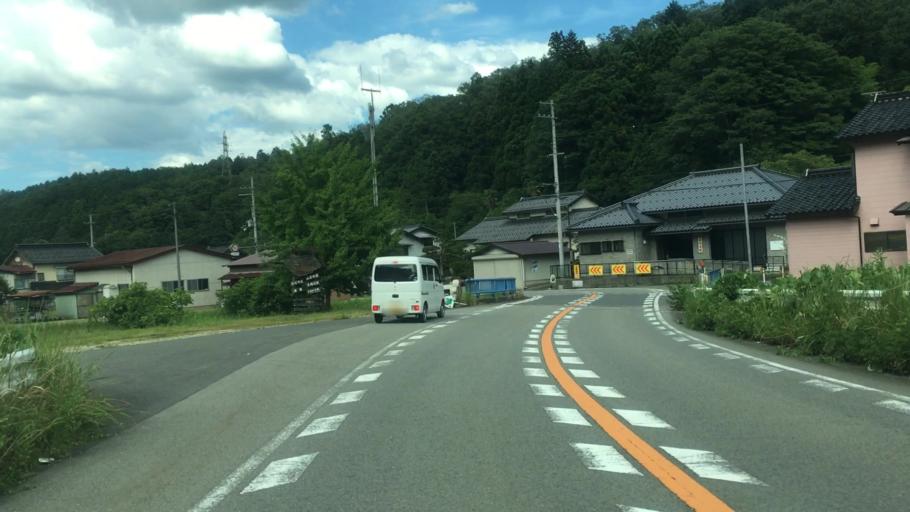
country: JP
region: Hyogo
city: Toyooka
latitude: 35.5352
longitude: 134.7891
